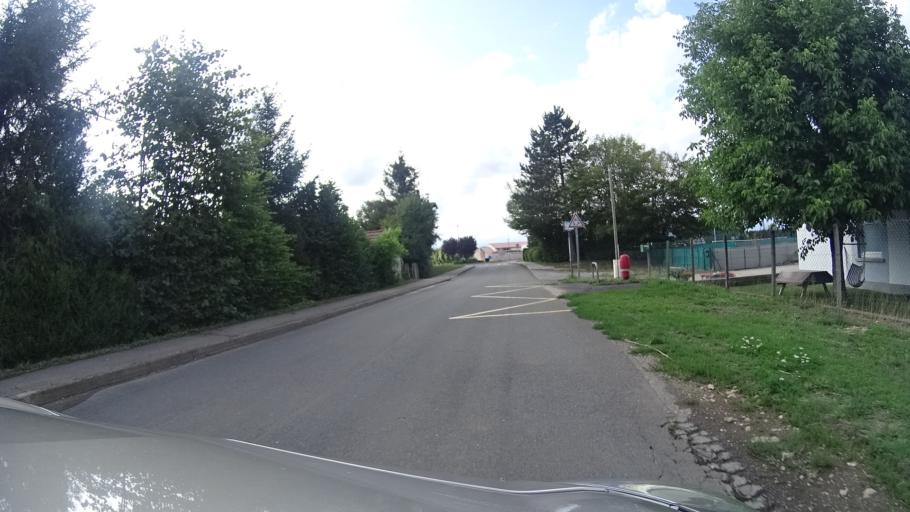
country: FR
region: Franche-Comte
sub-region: Departement du Doubs
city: Mamirolle
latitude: 47.2048
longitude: 6.1522
